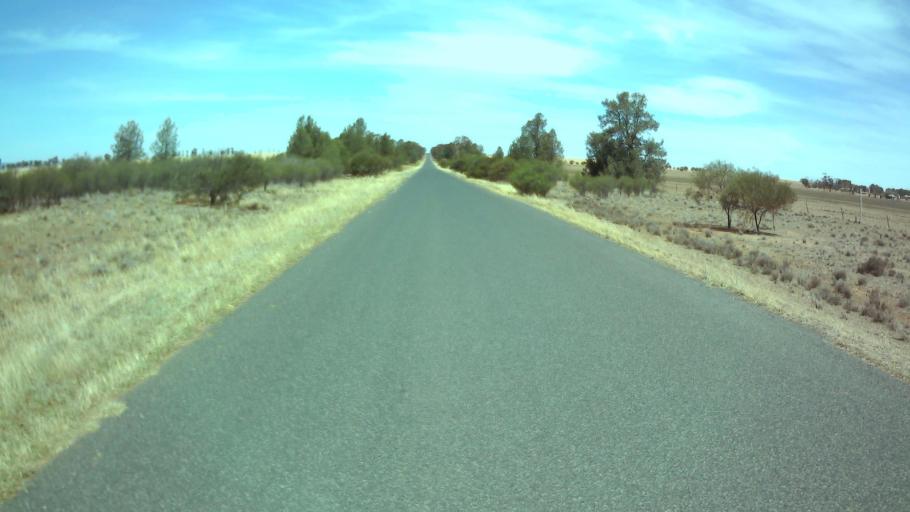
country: AU
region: New South Wales
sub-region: Weddin
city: Grenfell
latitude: -33.8904
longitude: 147.7432
